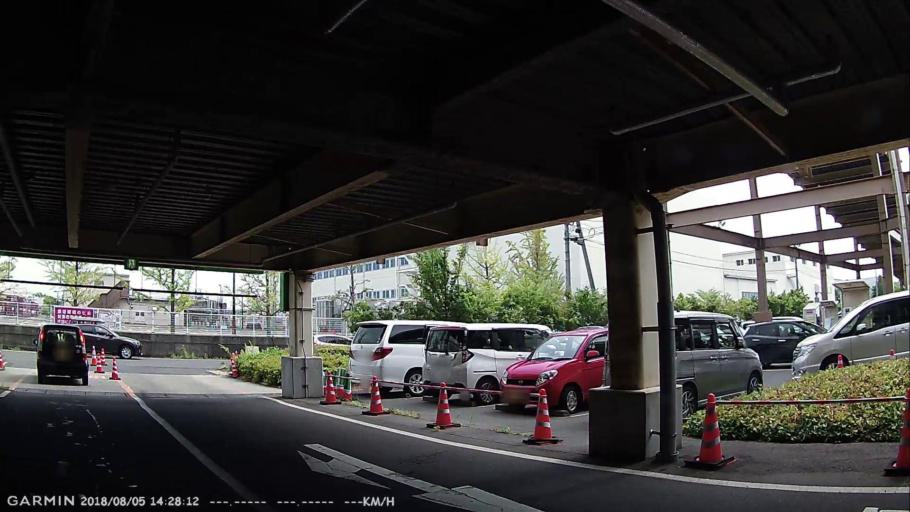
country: JP
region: Niigata
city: Kameda-honcho
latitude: 37.8747
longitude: 139.0821
